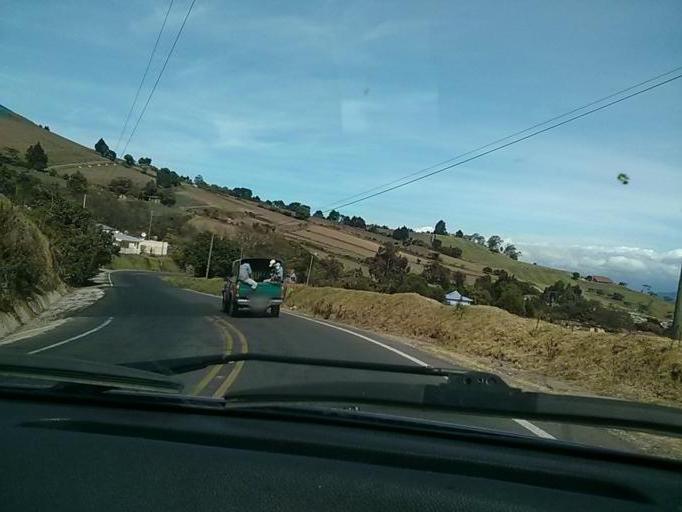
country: CR
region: Cartago
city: Cot
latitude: 9.9234
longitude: -83.8816
